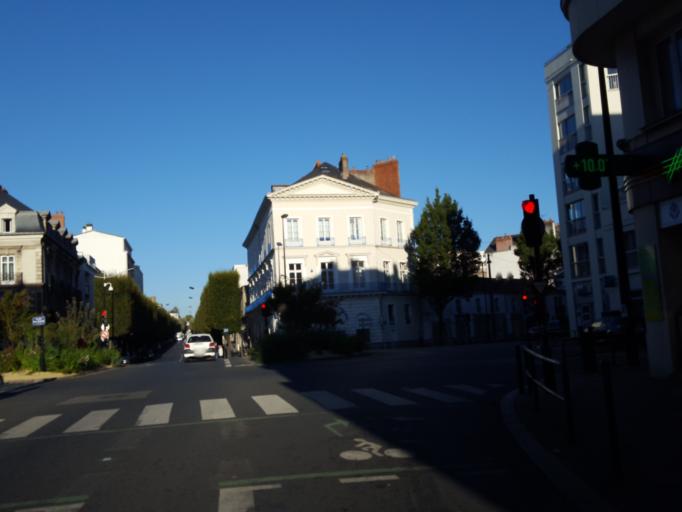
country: FR
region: Pays de la Loire
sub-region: Departement de la Loire-Atlantique
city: Nantes
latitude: 47.2095
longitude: -1.5700
